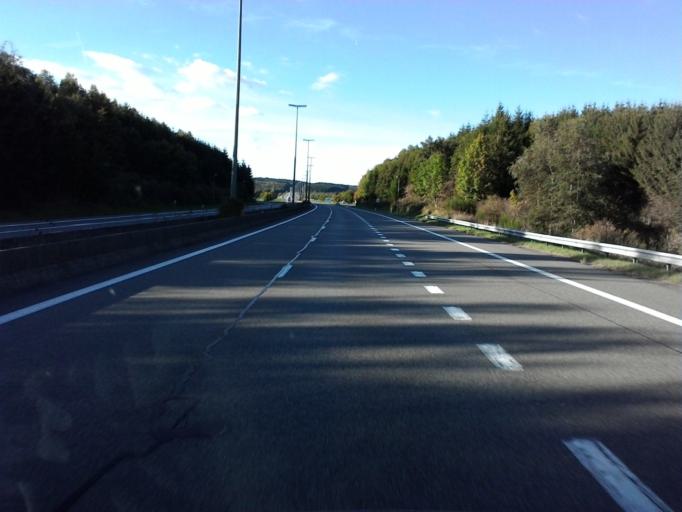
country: BE
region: Wallonia
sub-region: Province du Luxembourg
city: Houffalize
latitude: 50.1679
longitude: 5.7933
